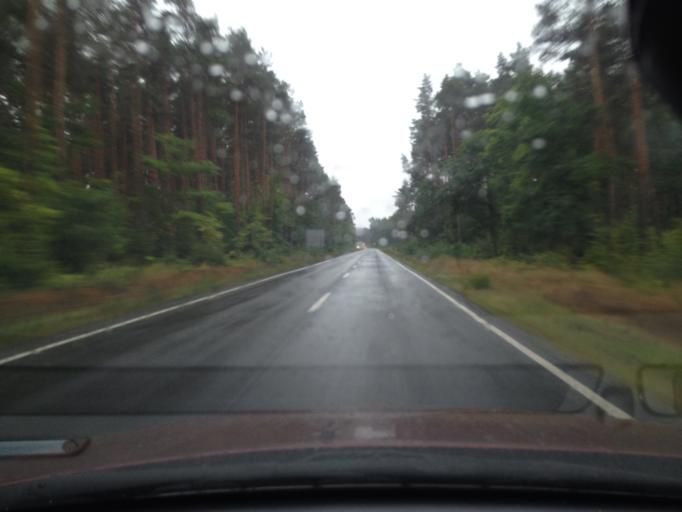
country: PL
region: Lubusz
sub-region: Powiat zaganski
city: Ilowa
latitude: 51.4779
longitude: 15.1989
